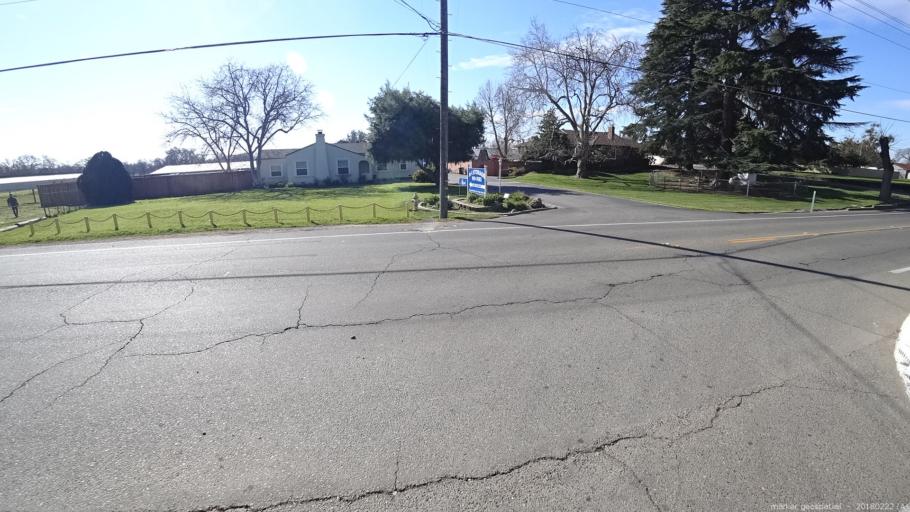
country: US
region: California
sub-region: Sacramento County
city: Rio Linda
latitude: 38.6982
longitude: -121.4338
